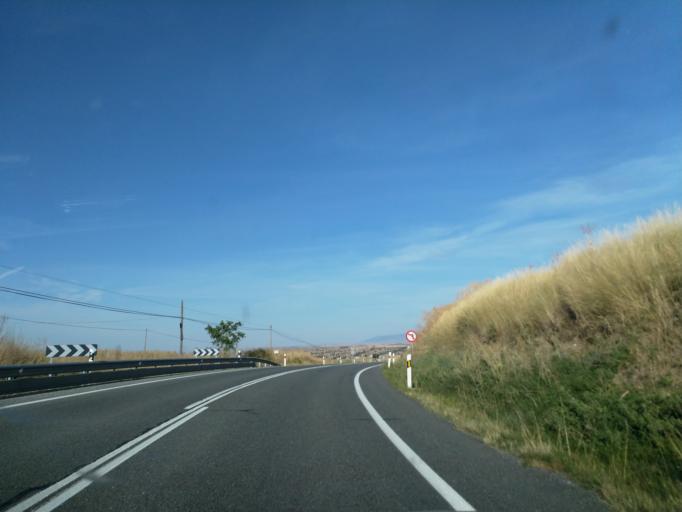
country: ES
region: Castille and Leon
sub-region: Provincia de Segovia
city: Villacastin
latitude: 40.7864
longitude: -4.4045
